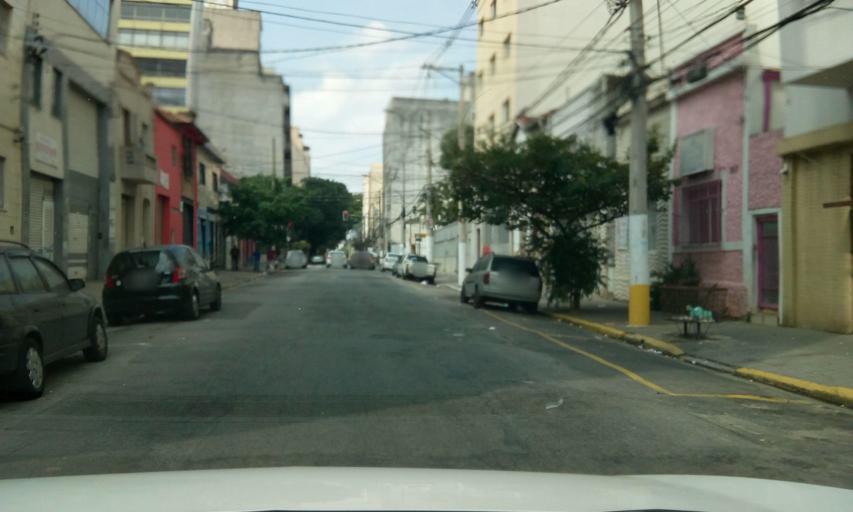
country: BR
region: Sao Paulo
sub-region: Sao Paulo
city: Sao Paulo
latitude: -23.5279
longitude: -46.6344
